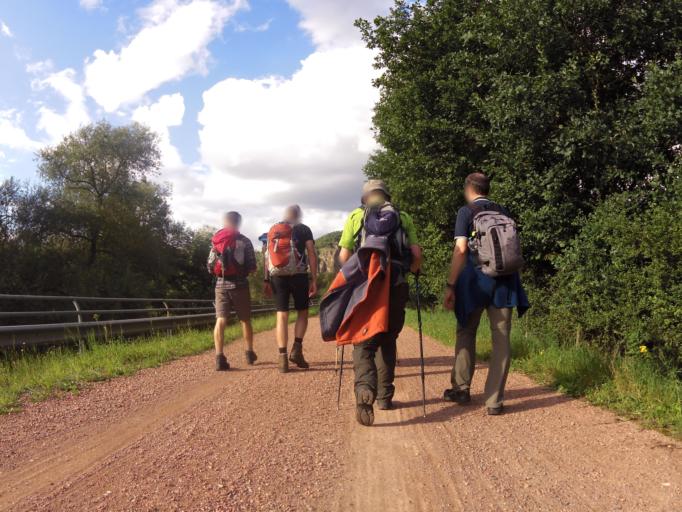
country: DE
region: Rheinland-Pfalz
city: Traisen
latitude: 49.8095
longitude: 7.8218
